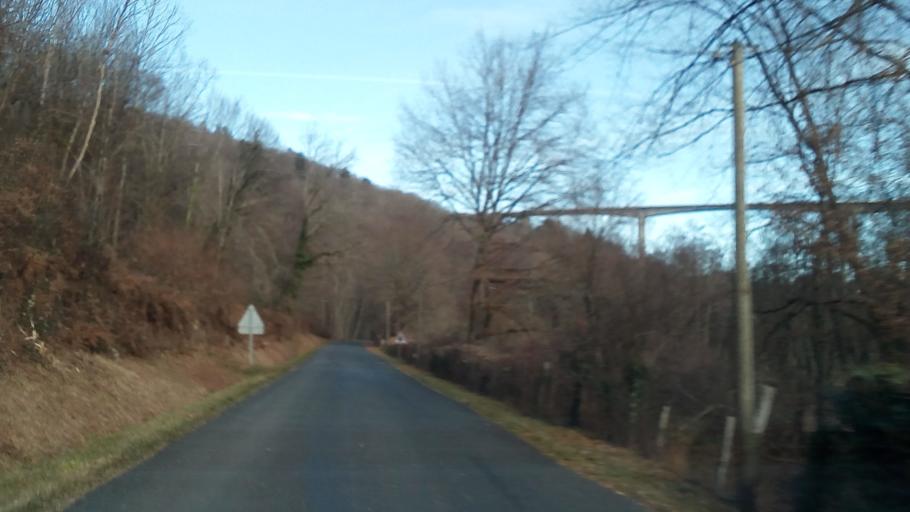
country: FR
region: Limousin
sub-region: Departement de la Correze
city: Naves
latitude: 45.3118
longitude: 1.7806
